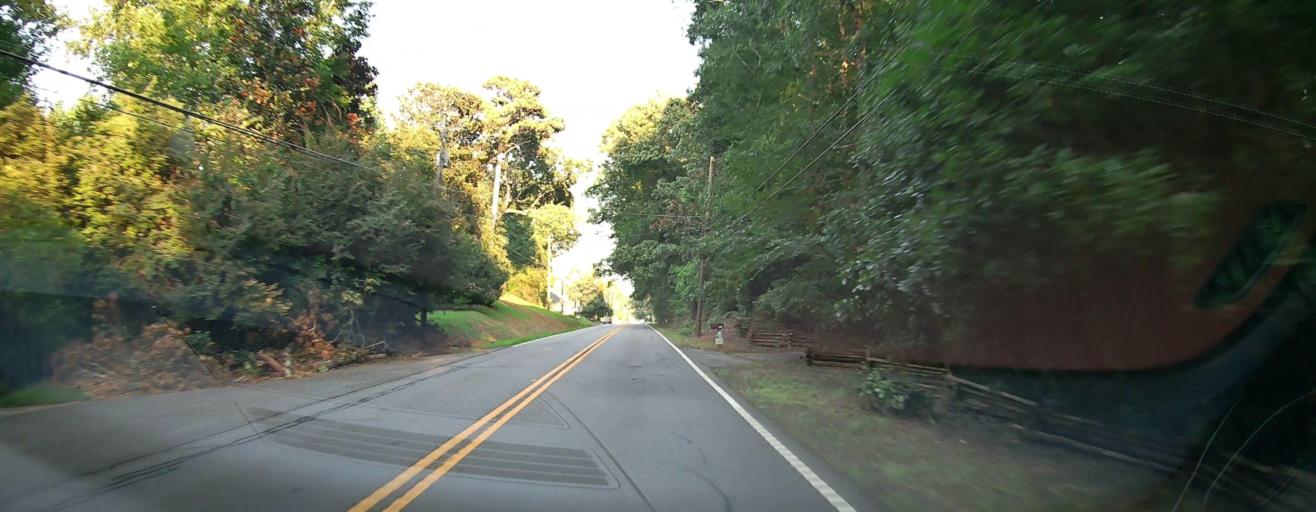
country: US
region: Georgia
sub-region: Bibb County
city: West Point
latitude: 32.8905
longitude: -83.7492
